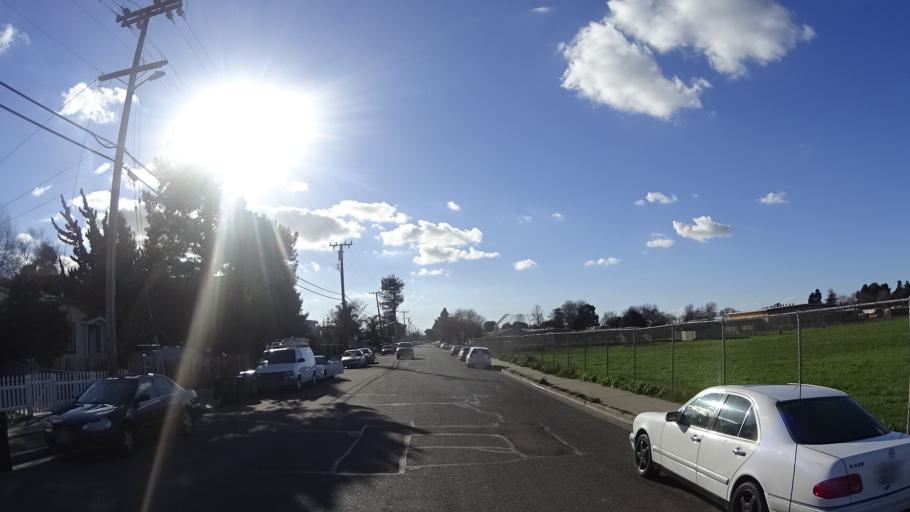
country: US
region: California
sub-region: Alameda County
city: Cherryland
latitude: 37.6723
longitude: -122.0944
